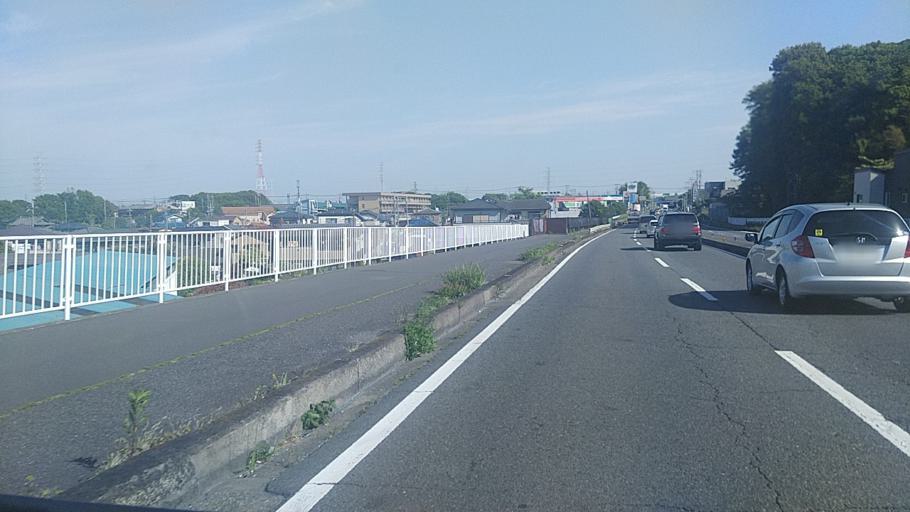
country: JP
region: Saitama
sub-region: Kawaguchi-shi
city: Hatogaya-honcho
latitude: 35.8431
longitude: 139.7344
